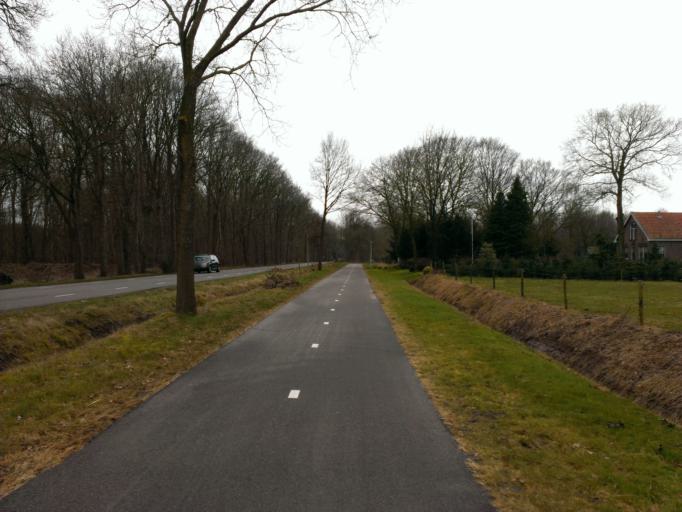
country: NL
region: Drenthe
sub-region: Gemeente Hoogeveen
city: Hoogeveen
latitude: 52.7596
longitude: 6.4590
